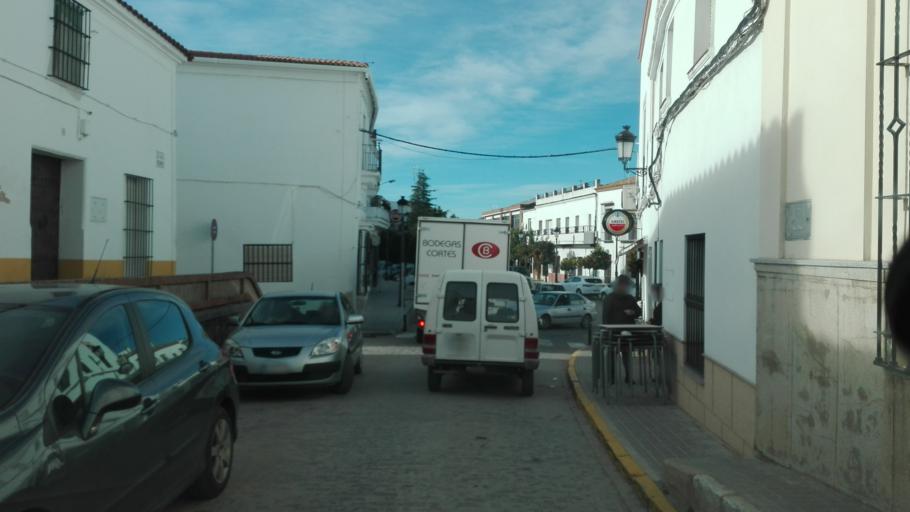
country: ES
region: Extremadura
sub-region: Provincia de Badajoz
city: Usagre
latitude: 38.3580
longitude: -6.1648
